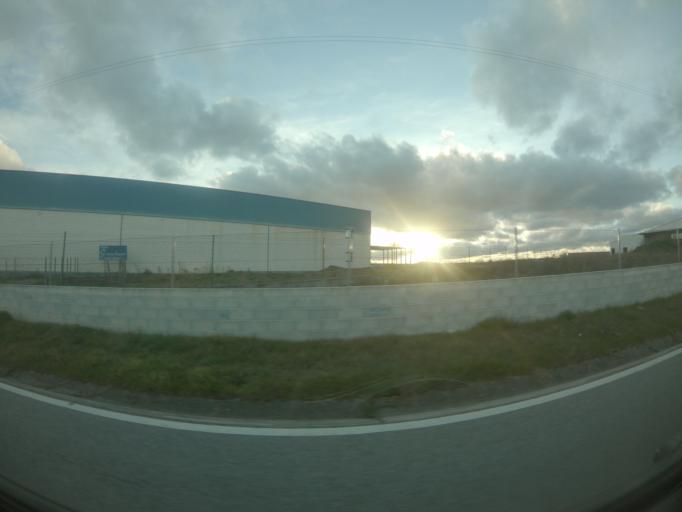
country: PT
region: Braganca
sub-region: Carrazeda de Ansiaes
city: Carrazeda de Anciaes
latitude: 41.2340
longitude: -7.3046
